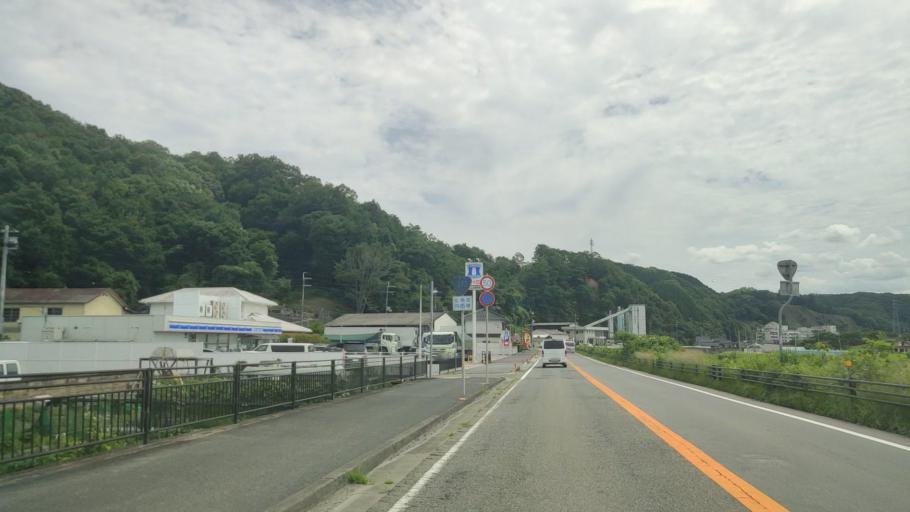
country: JP
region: Hyogo
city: Yamazakicho-nakabirose
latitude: 35.0153
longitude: 134.3697
